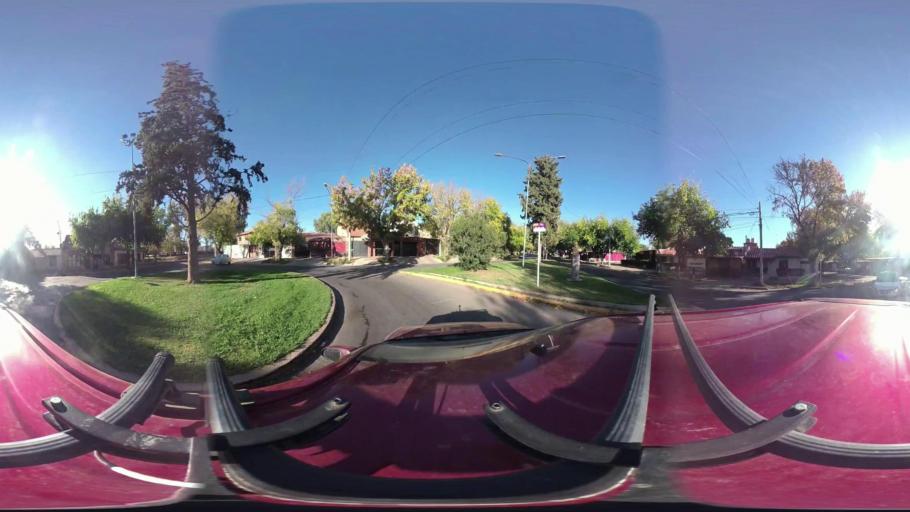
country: AR
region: Mendoza
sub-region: Departamento de Godoy Cruz
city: Godoy Cruz
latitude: -32.9054
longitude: -68.8572
